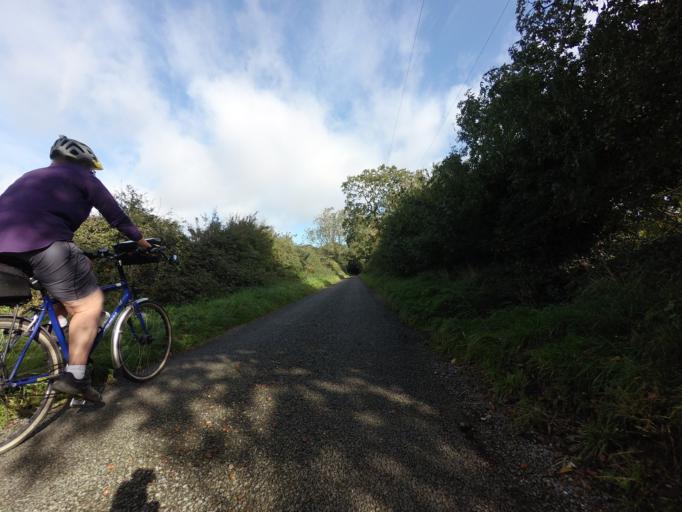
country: GB
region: England
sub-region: Norfolk
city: Dersingham
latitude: 52.8659
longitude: 0.6667
